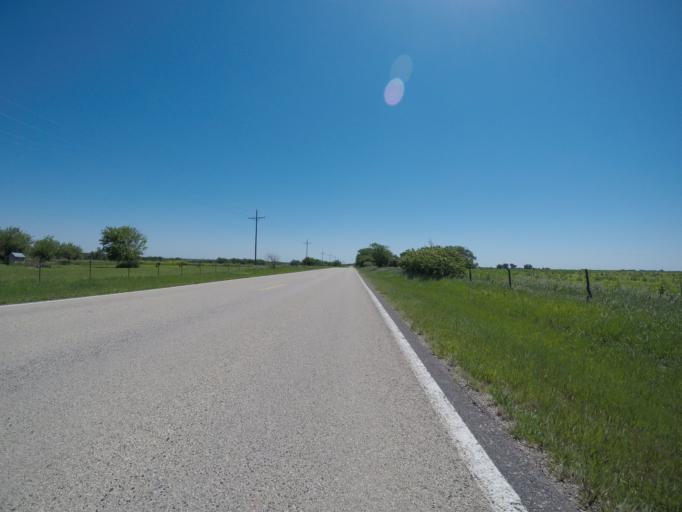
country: US
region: Kansas
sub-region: Shawnee County
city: Auburn
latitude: 38.8846
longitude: -95.9733
